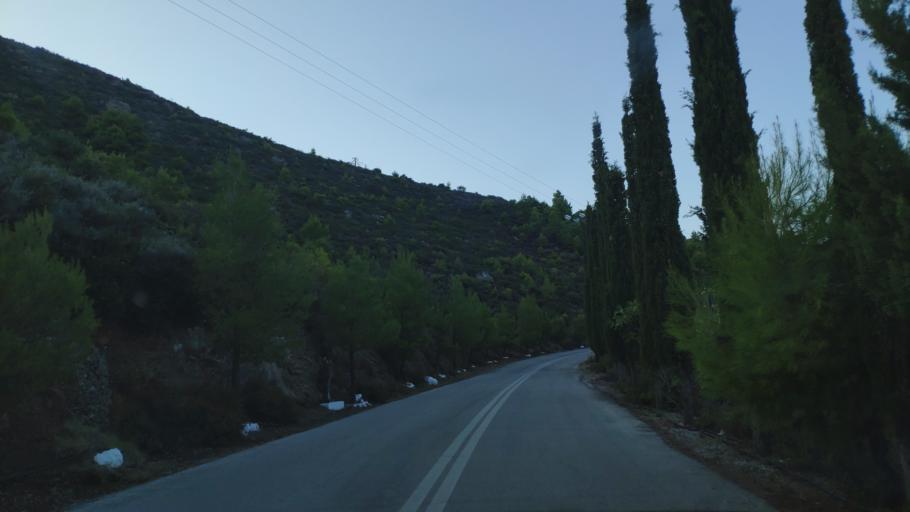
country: GR
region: West Greece
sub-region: Nomos Achaias
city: Aiyira
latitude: 38.0895
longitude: 22.4086
